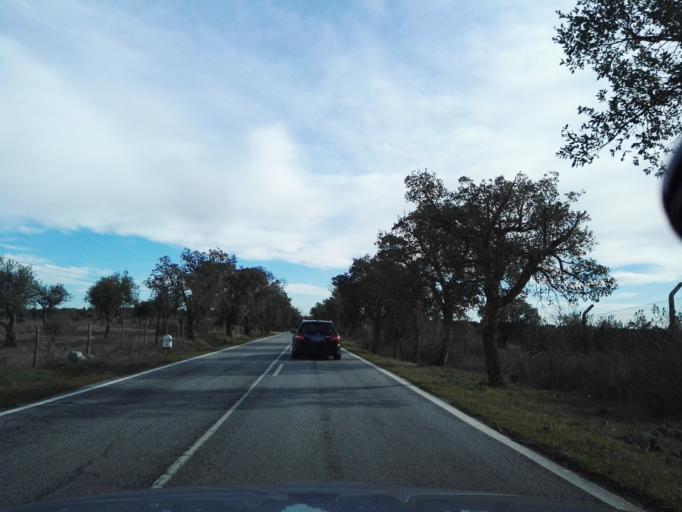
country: PT
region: Portalegre
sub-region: Nisa
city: Nisa
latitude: 39.4990
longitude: -7.6924
